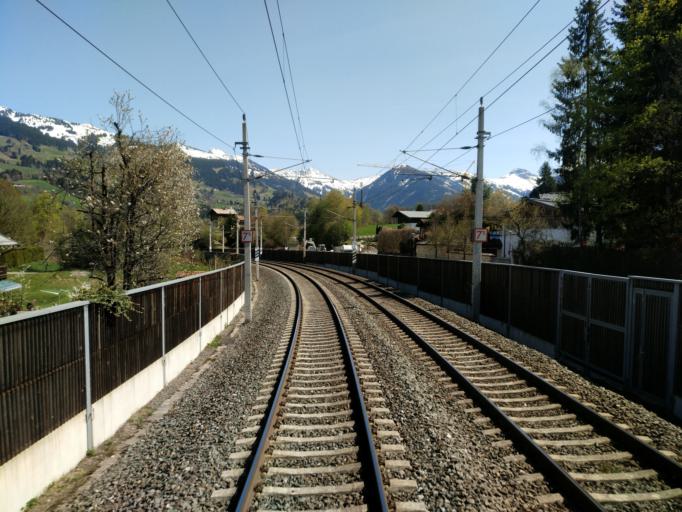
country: AT
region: Tyrol
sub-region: Politischer Bezirk Kitzbuhel
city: Kitzbuhel
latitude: 47.4414
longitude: 12.3938
